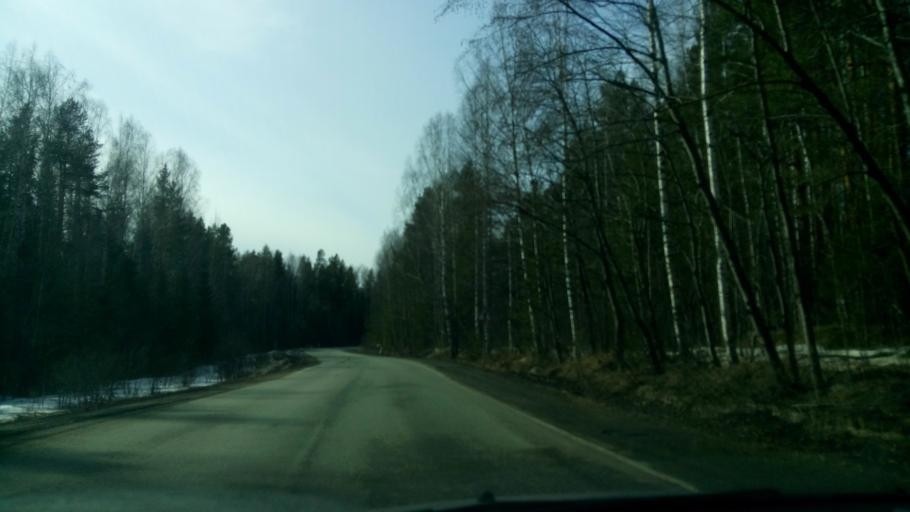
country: RU
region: Sverdlovsk
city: Chernoistochinsk
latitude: 57.7013
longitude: 59.7705
